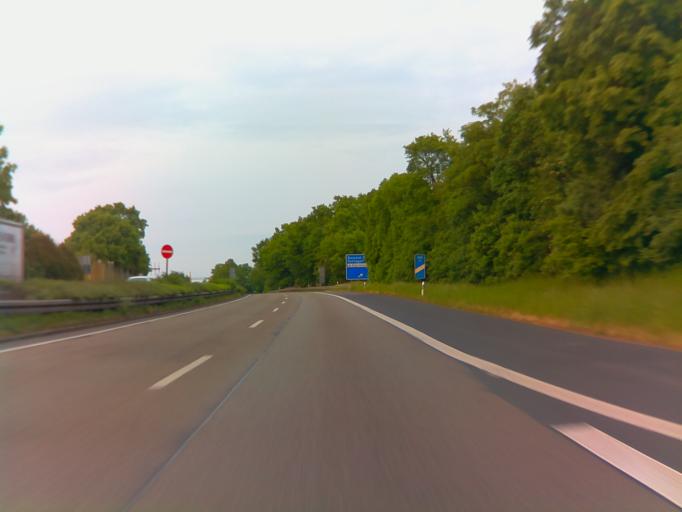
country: DE
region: Hesse
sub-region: Regierungsbezirk Kassel
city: Baunatal
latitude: 51.2257
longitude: 9.4228
